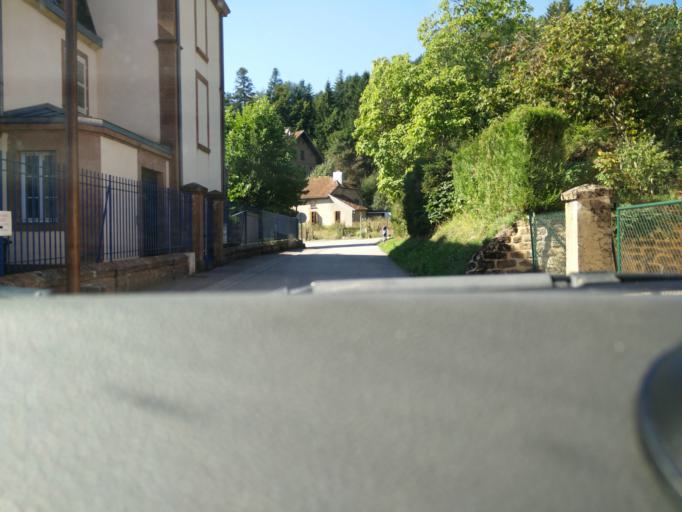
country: FR
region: Lorraine
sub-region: Departement des Vosges
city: Senones
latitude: 48.4623
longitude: 6.9486
